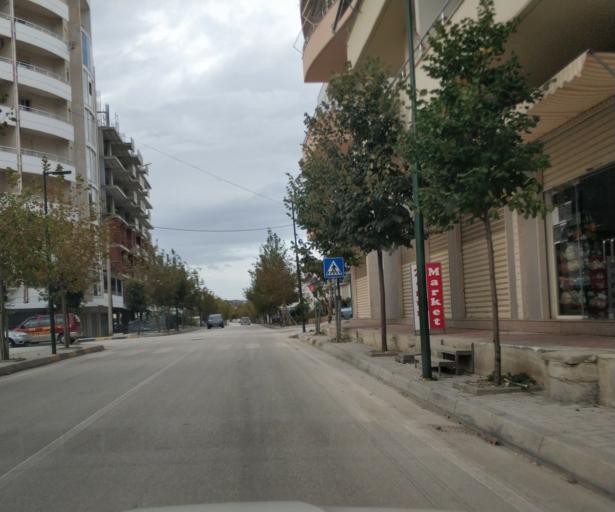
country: AL
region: Vlore
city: Vlore
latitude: 40.4419
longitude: 19.4974
